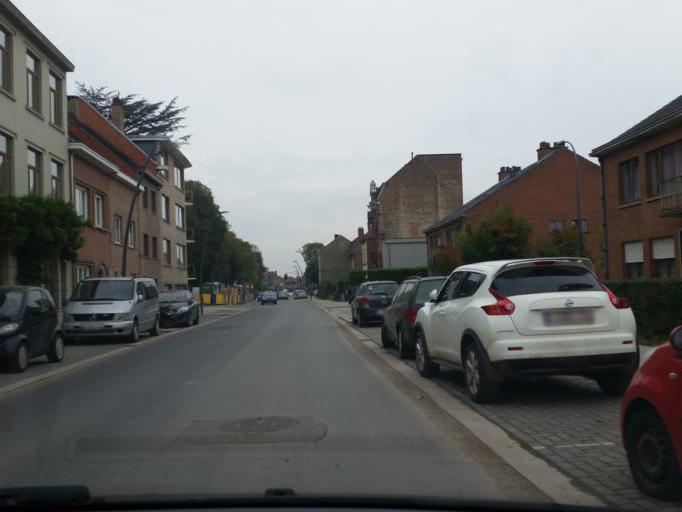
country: BE
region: Flanders
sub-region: Provincie Vlaams-Brabant
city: Drogenbos
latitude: 50.7834
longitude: 4.3198
